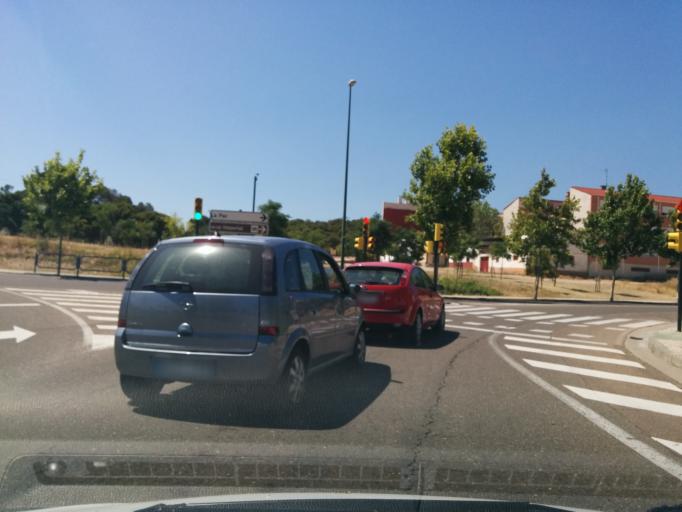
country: ES
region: Aragon
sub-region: Provincia de Zaragoza
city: Zaragoza
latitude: 41.6212
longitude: -0.8760
